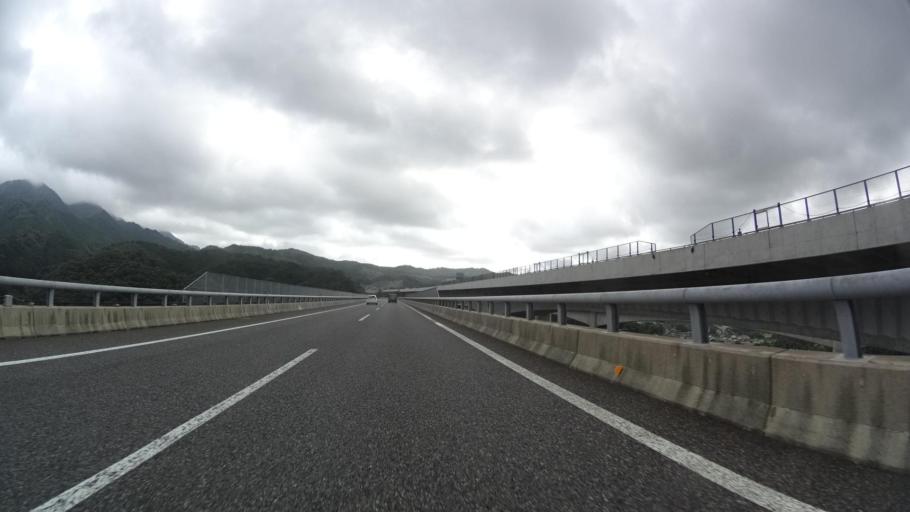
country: JP
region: Mie
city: Kameyama
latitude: 34.9174
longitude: 136.4035
